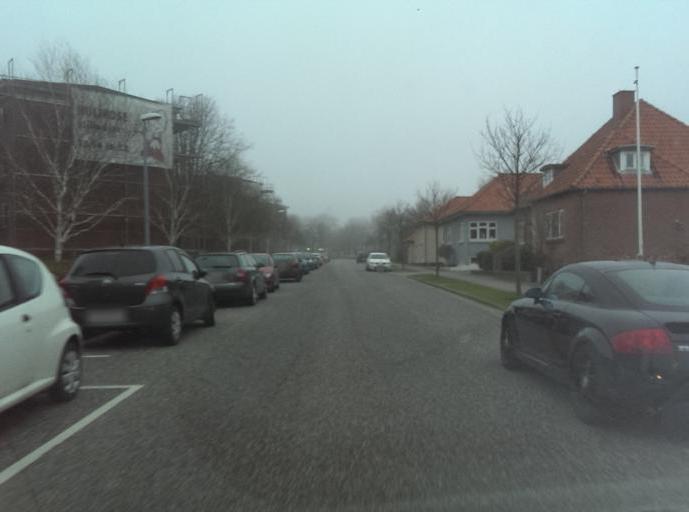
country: DK
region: South Denmark
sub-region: Esbjerg Kommune
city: Esbjerg
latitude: 55.4763
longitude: 8.4397
